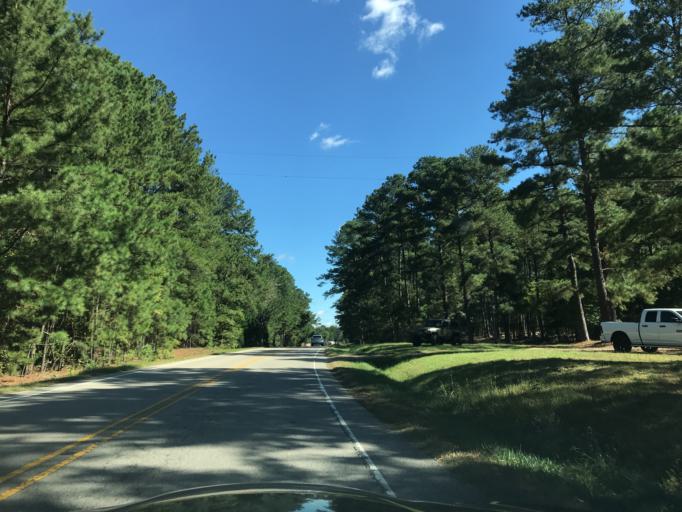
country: US
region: North Carolina
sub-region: Wake County
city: Wake Forest
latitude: 35.9245
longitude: -78.5161
